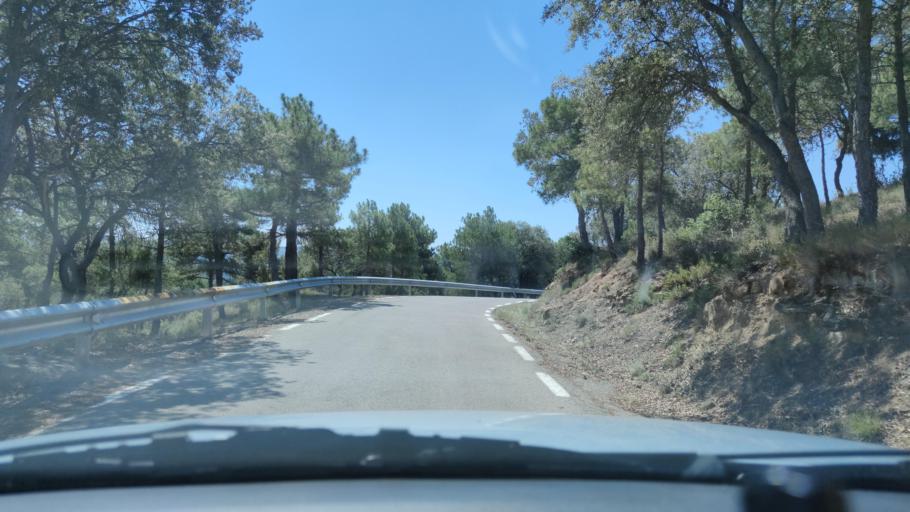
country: ES
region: Catalonia
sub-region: Provincia de Lleida
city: Tora de Riubregos
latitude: 41.8606
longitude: 1.4340
